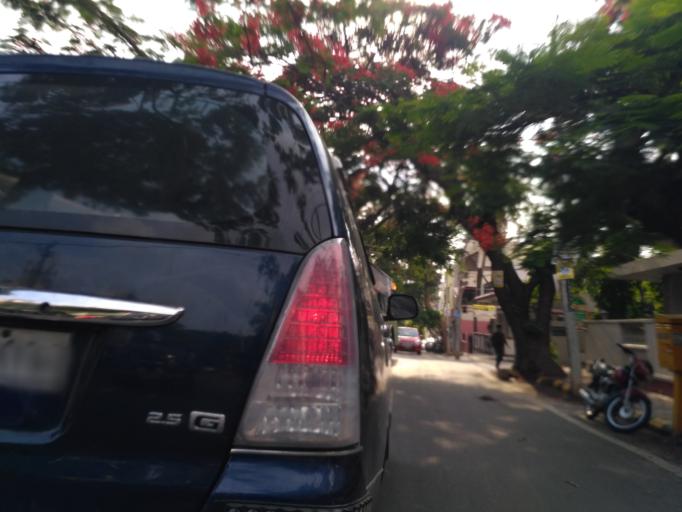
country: IN
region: Karnataka
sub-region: Bangalore Urban
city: Bangalore
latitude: 12.9737
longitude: 77.5366
